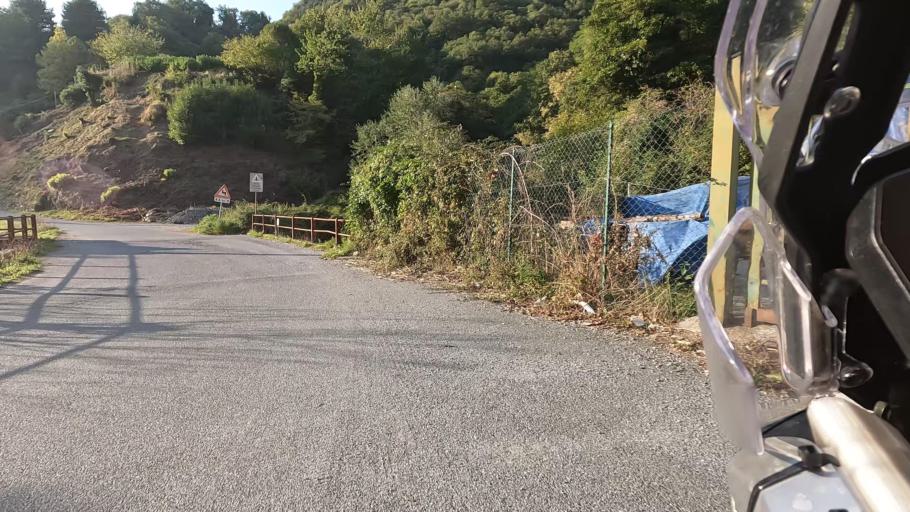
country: IT
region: Liguria
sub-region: Provincia di Savona
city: San Giovanni
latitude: 44.4035
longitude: 8.5324
